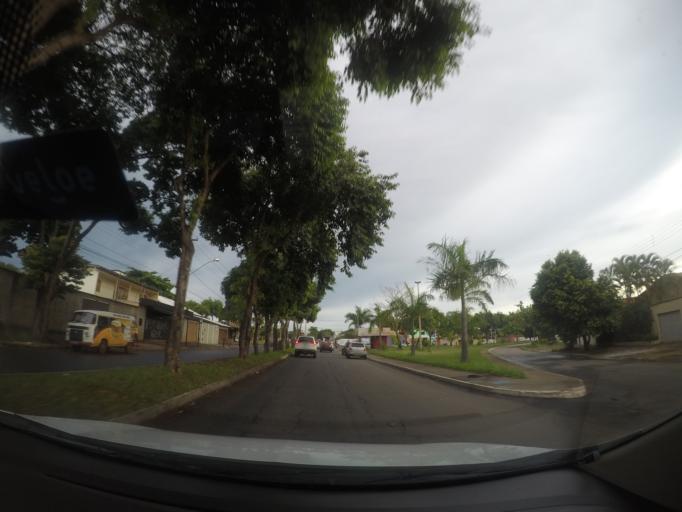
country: BR
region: Goias
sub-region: Goiania
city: Goiania
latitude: -16.7163
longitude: -49.3105
